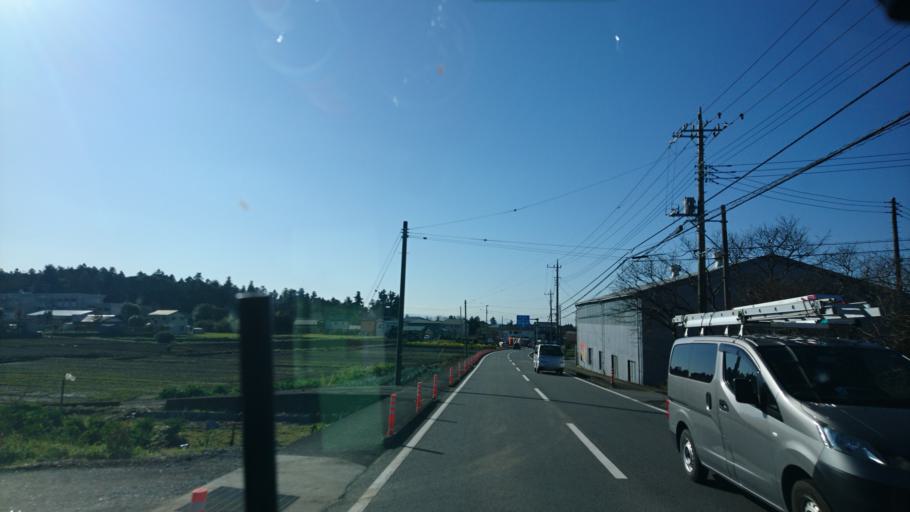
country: JP
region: Shizuoka
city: Fujinomiya
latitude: 35.2798
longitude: 138.6044
